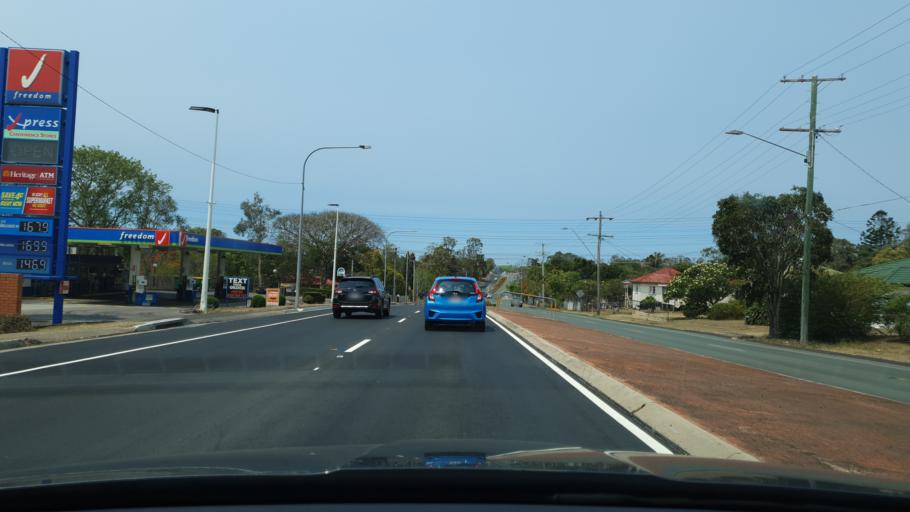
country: AU
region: Queensland
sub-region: Ipswich
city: Bundamba
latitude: -27.6015
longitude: 152.8260
